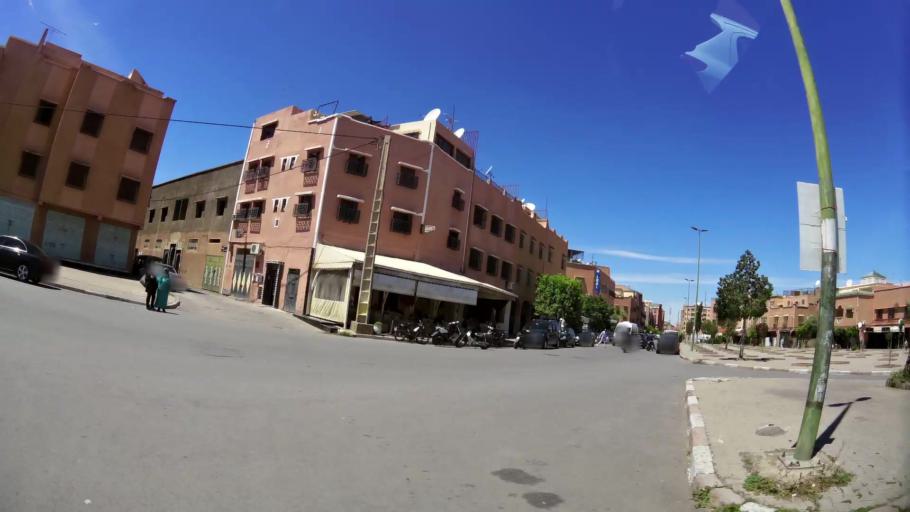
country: MA
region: Marrakech-Tensift-Al Haouz
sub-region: Marrakech
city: Marrakesh
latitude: 31.6306
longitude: -8.0506
